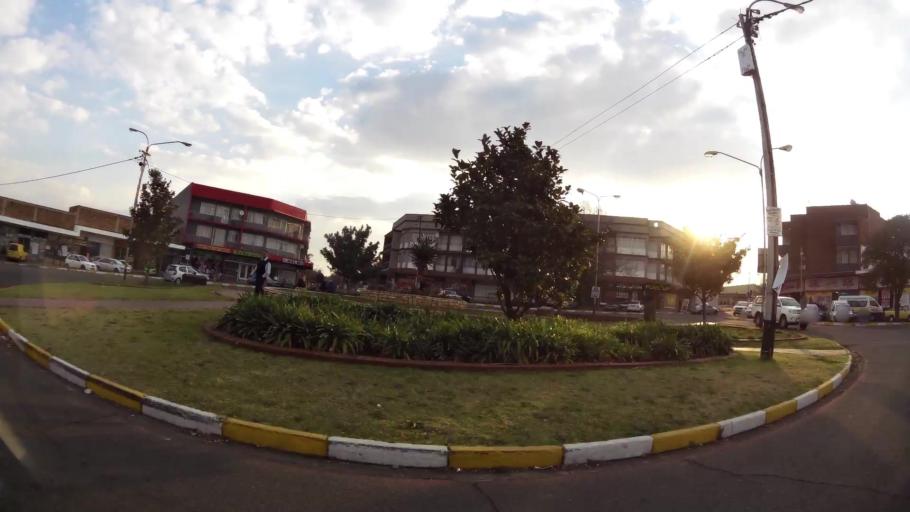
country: ZA
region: Gauteng
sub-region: Ekurhuleni Metropolitan Municipality
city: Germiston
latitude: -26.1720
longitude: 28.1769
